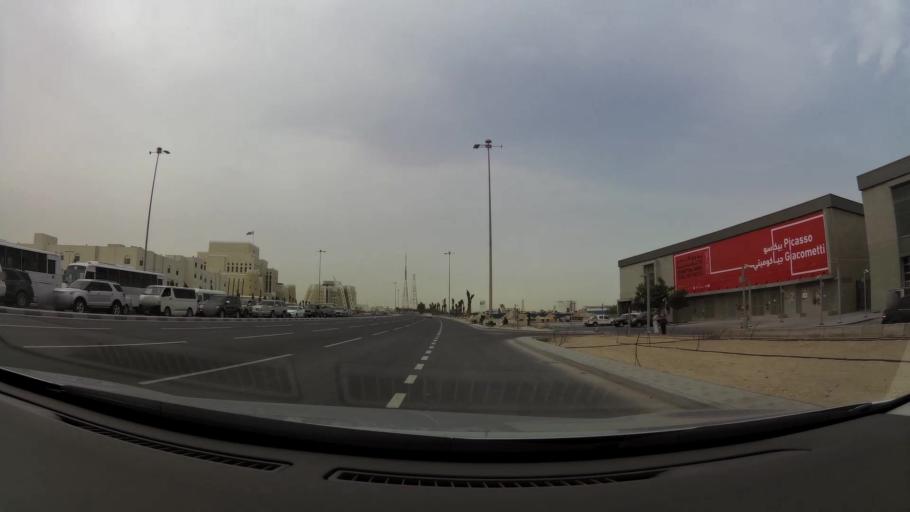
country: QA
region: Baladiyat ad Dawhah
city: Doha
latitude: 25.3026
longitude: 51.5071
